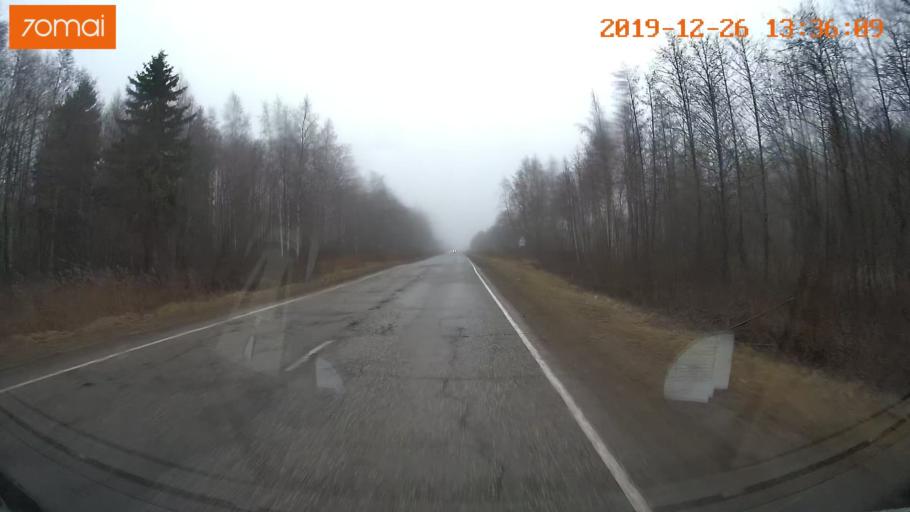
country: RU
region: Vologda
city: Sheksna
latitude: 58.7858
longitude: 38.3507
